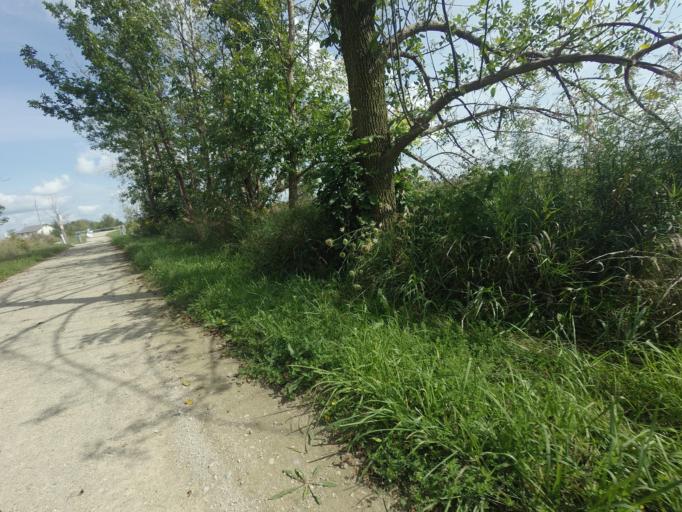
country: CA
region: Ontario
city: Waterloo
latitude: 43.5895
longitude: -80.6964
